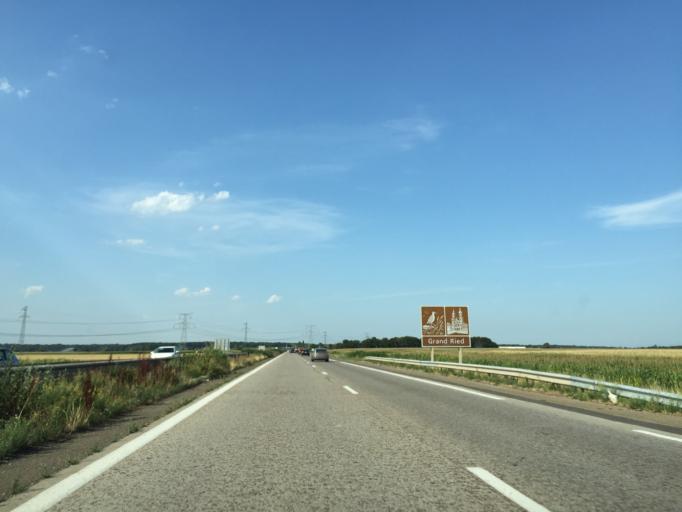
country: FR
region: Alsace
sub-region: Departement du Bas-Rhin
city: Ebersheim
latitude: 48.3035
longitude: 7.4731
